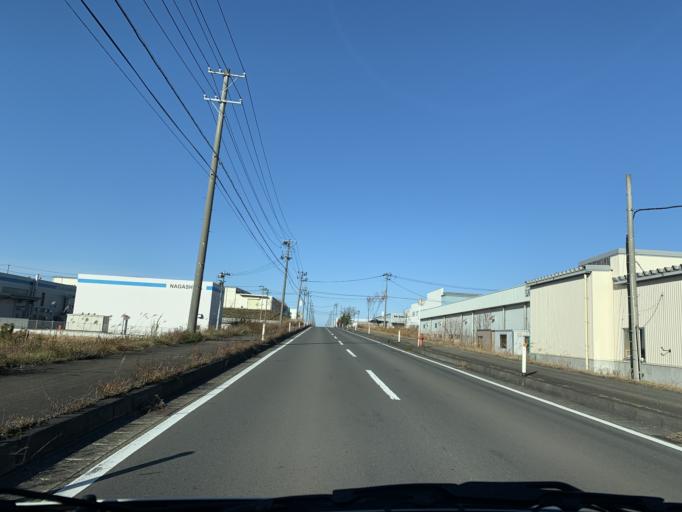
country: JP
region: Iwate
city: Kitakami
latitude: 39.2407
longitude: 141.0925
